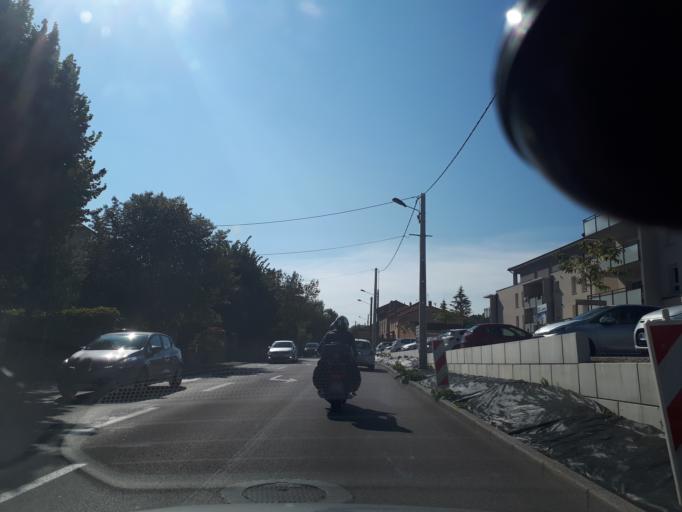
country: FR
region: Rhone-Alpes
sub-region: Departement de l'Isere
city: Bourgoin-Jallieu
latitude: 45.5793
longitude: 5.2746
